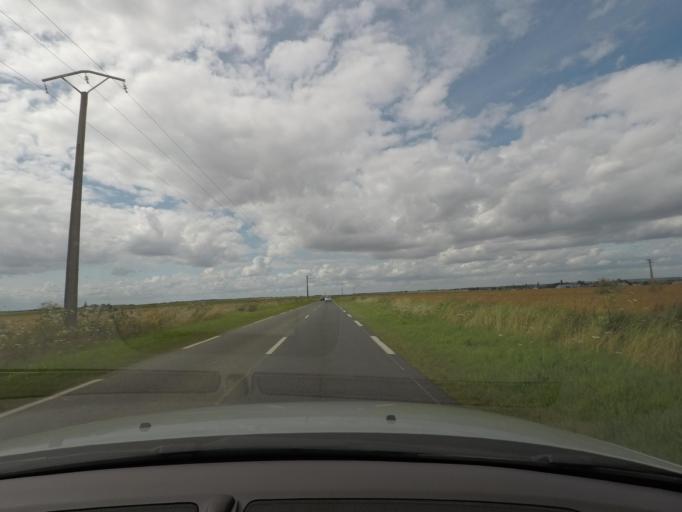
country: FR
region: Haute-Normandie
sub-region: Departement de l'Eure
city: Les Andelys
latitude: 49.2046
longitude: 1.4675
